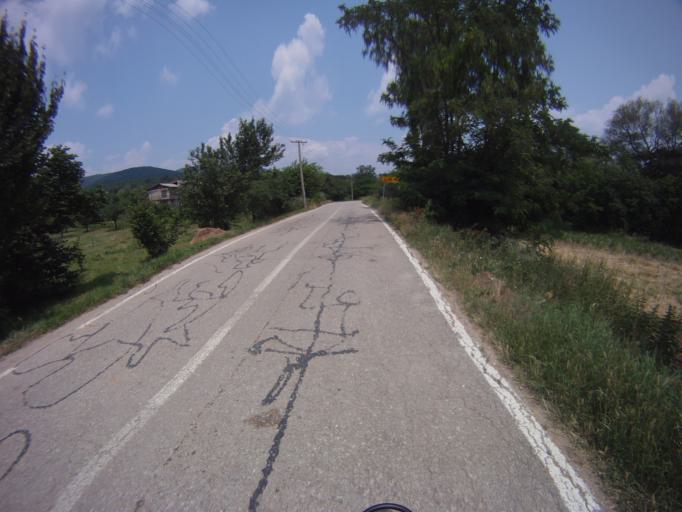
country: RS
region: Central Serbia
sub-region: Nisavski Okrug
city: Gadzin Han
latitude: 43.2042
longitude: 21.9644
